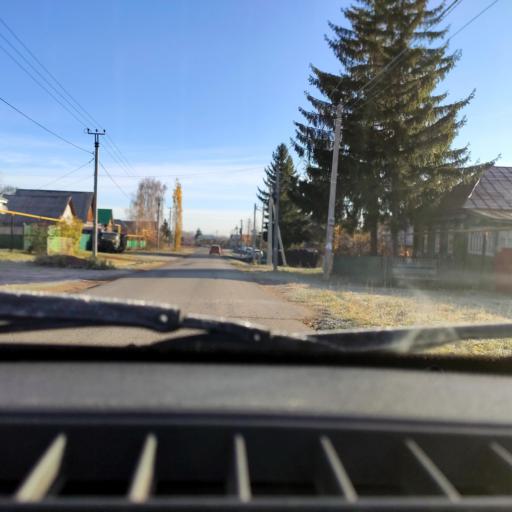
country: RU
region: Bashkortostan
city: Avdon
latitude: 54.6406
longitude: 55.7361
